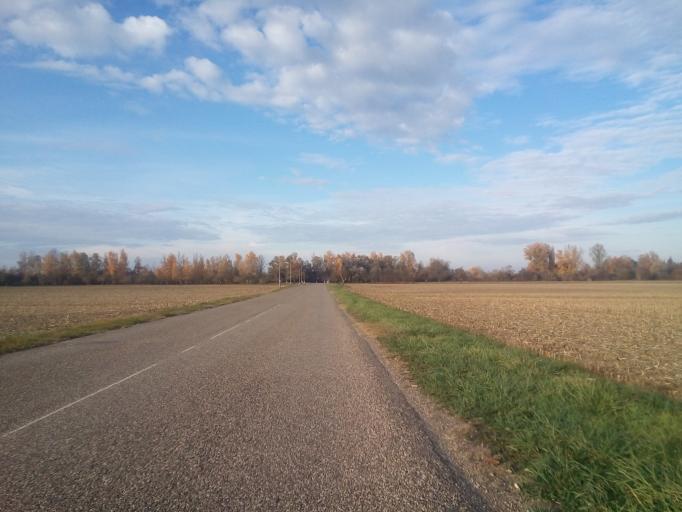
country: FR
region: Alsace
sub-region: Departement du Bas-Rhin
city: Herrlisheim
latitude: 48.6997
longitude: 7.9210
